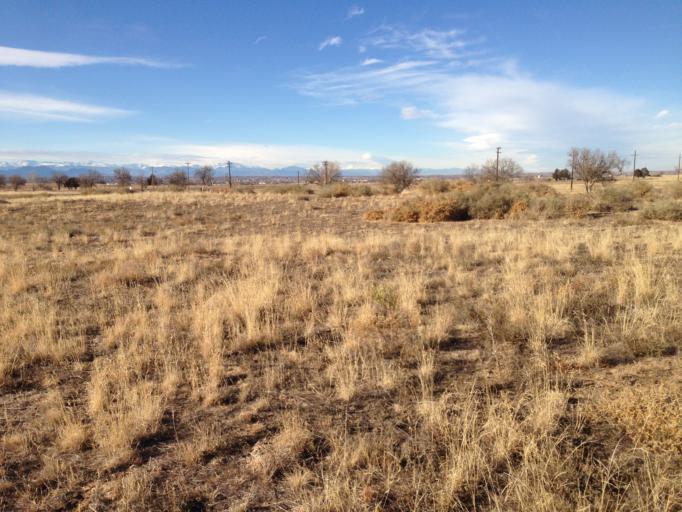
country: US
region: Colorado
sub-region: Adams County
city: Derby
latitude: 39.8259
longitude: -104.8633
